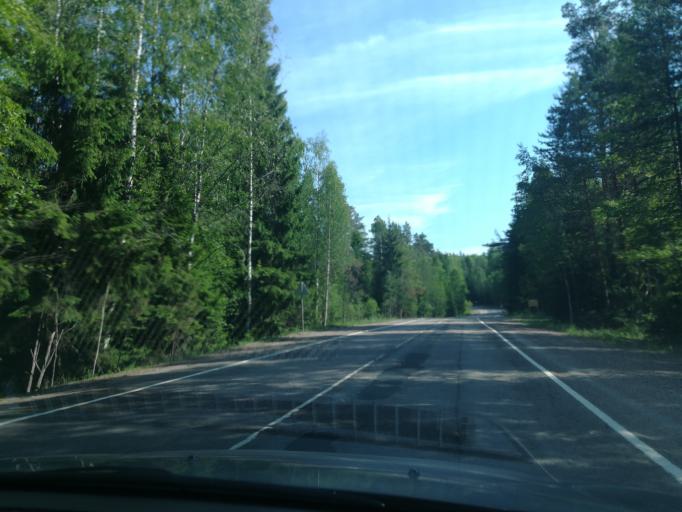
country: RU
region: Leningrad
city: Lesogorskiy
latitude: 60.9032
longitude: 28.8695
